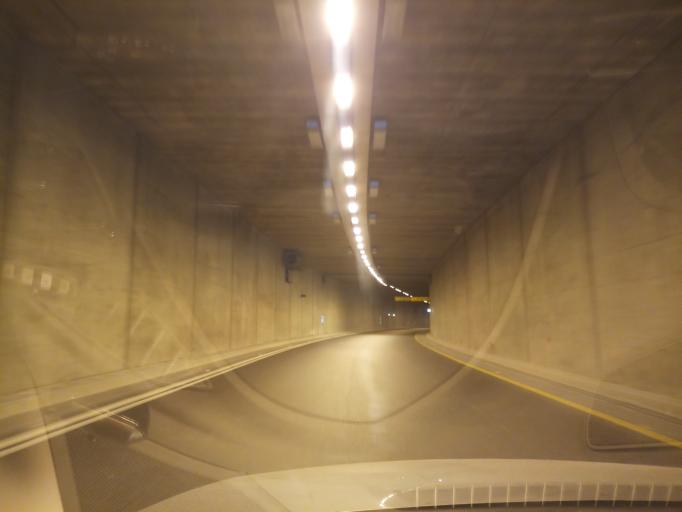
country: IL
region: Jerusalem
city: Jerusalem
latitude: 31.7652
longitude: 35.1933
